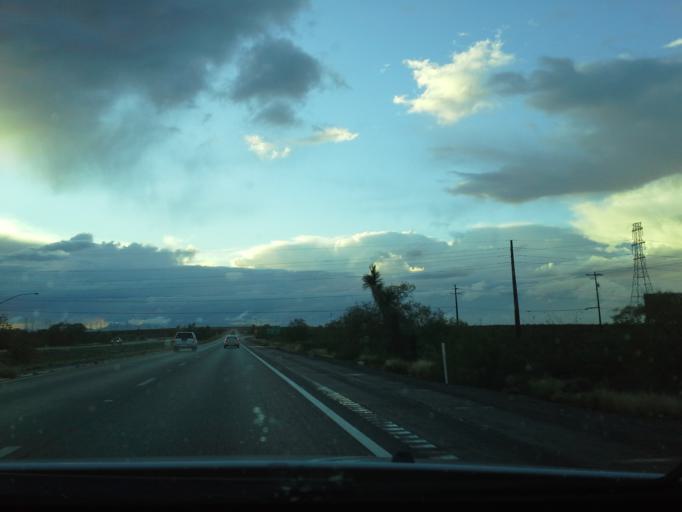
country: US
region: Arizona
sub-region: Pima County
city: Vail
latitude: 32.0579
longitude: -110.7675
